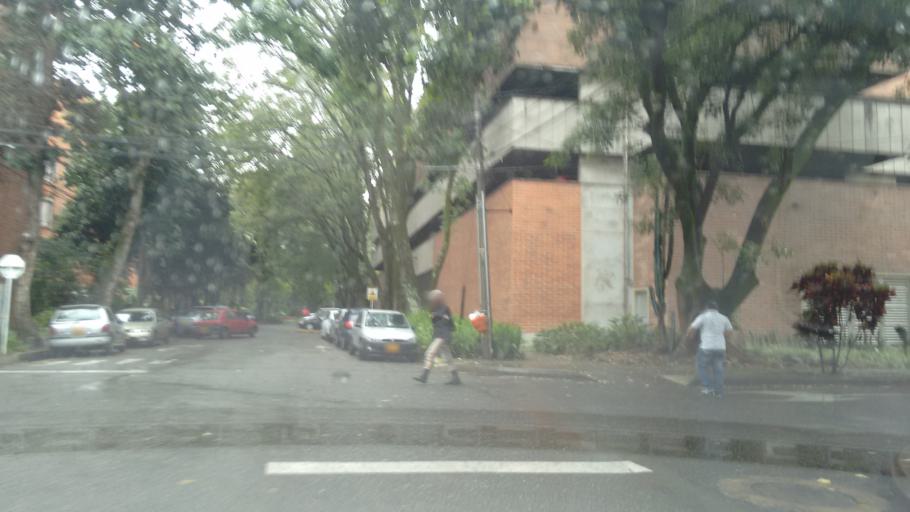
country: CO
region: Antioquia
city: Medellin
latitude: 6.2563
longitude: -75.5778
